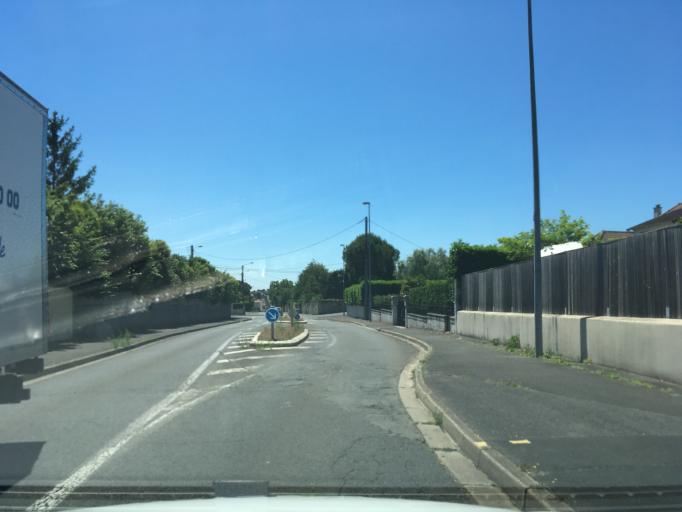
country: FR
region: Poitou-Charentes
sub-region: Departement des Deux-Sevres
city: Niort
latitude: 46.3428
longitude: -0.4427
